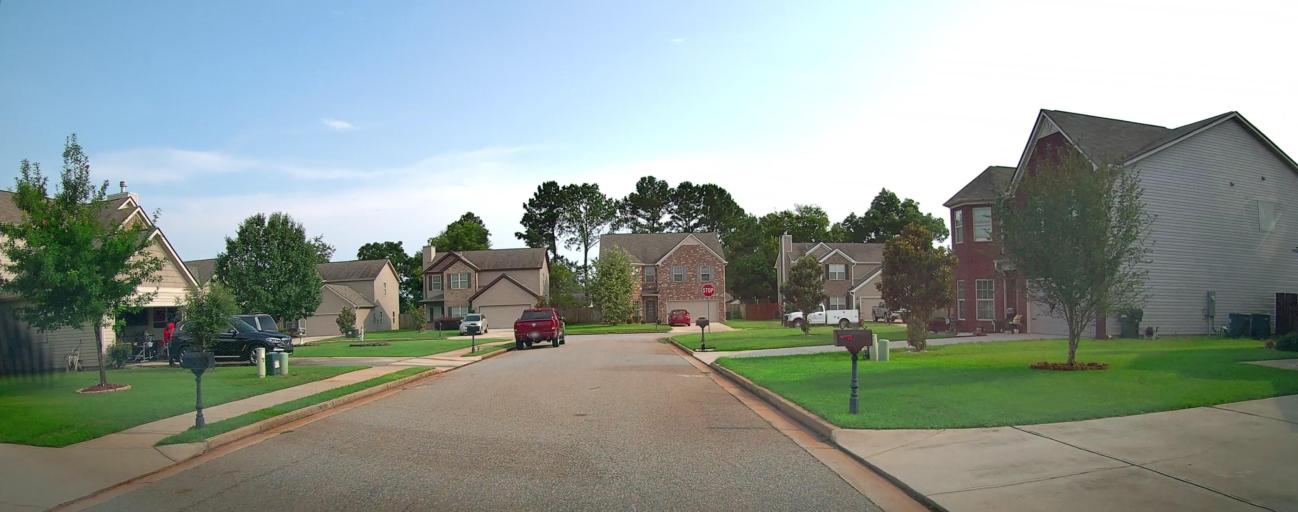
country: US
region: Georgia
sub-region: Houston County
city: Centerville
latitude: 32.6442
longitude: -83.7141
